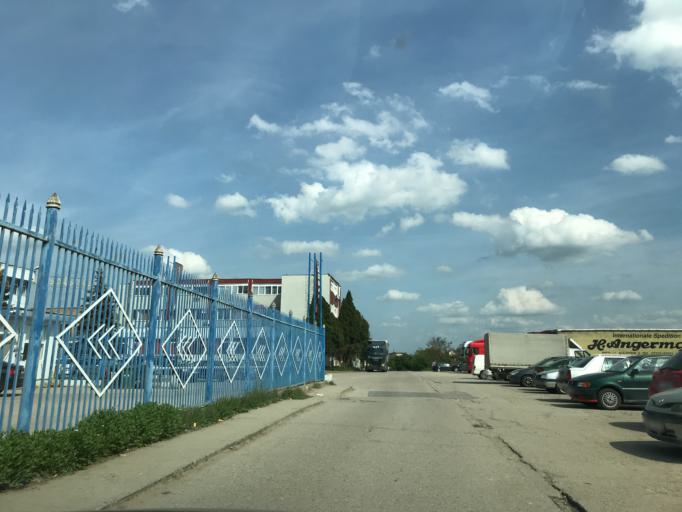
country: RO
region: Cluj
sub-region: Municipiul Cluj-Napoca
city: Cluj-Napoca
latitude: 46.7842
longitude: 23.6360
